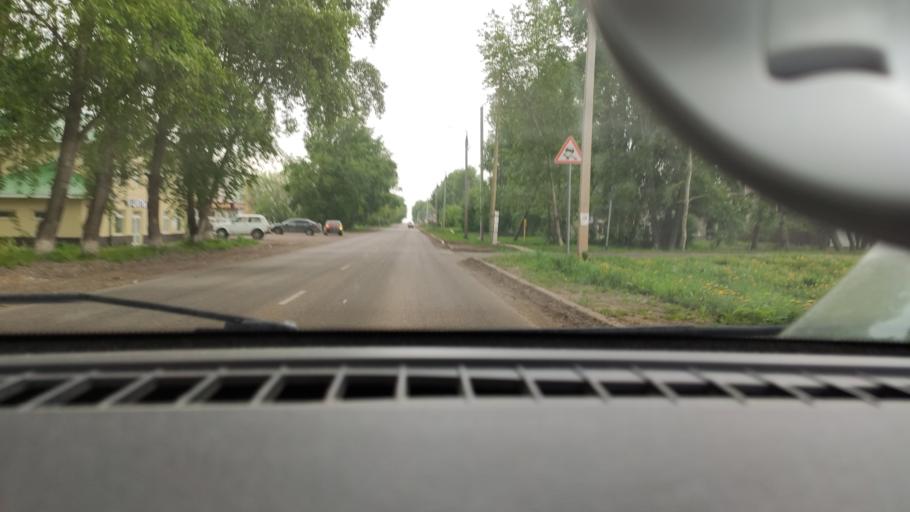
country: RU
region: Perm
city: Gamovo
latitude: 57.8697
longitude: 56.1022
